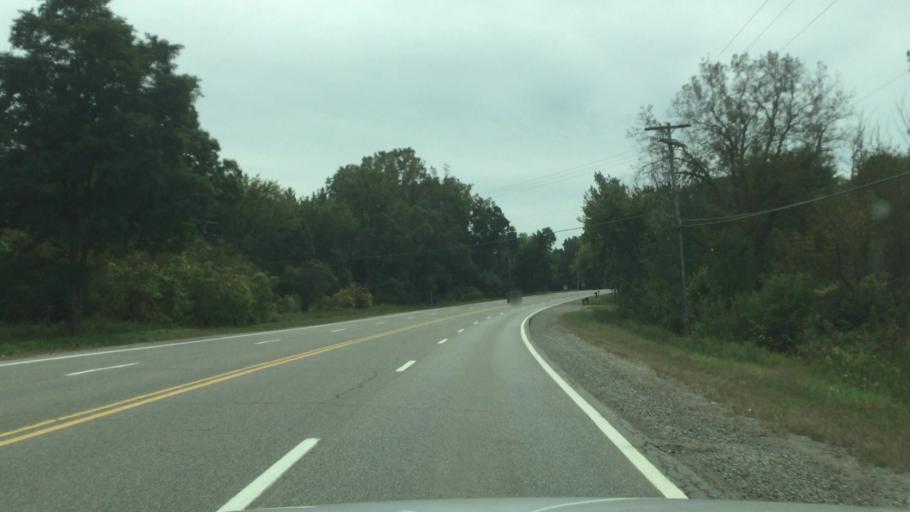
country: US
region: Michigan
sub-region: Oakland County
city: Holly
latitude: 42.8083
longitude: -83.5366
